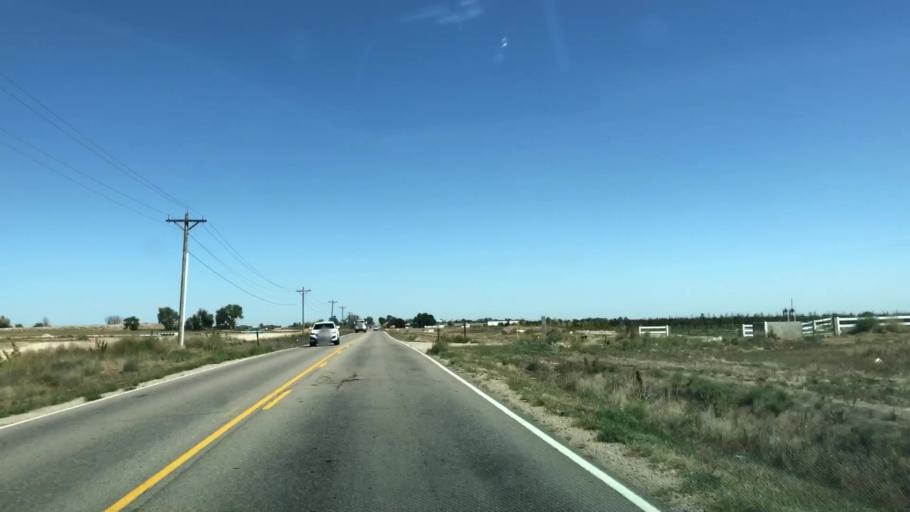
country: US
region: Colorado
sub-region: Weld County
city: Windsor
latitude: 40.5228
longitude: -104.9399
